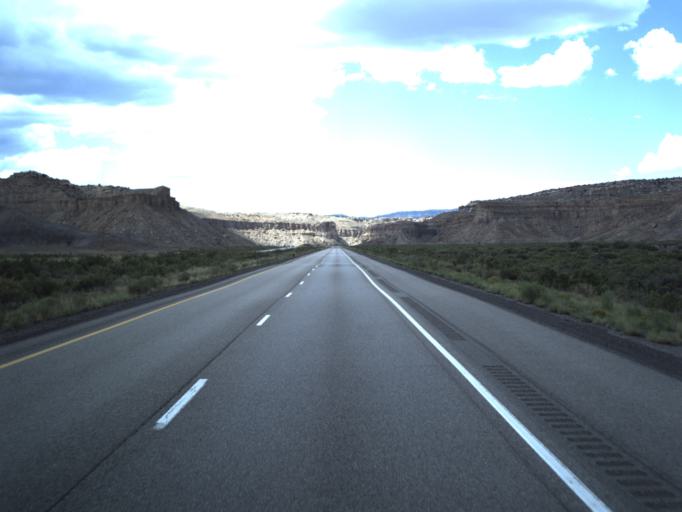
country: US
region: Utah
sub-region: Emery County
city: Ferron
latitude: 38.8099
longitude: -111.2338
